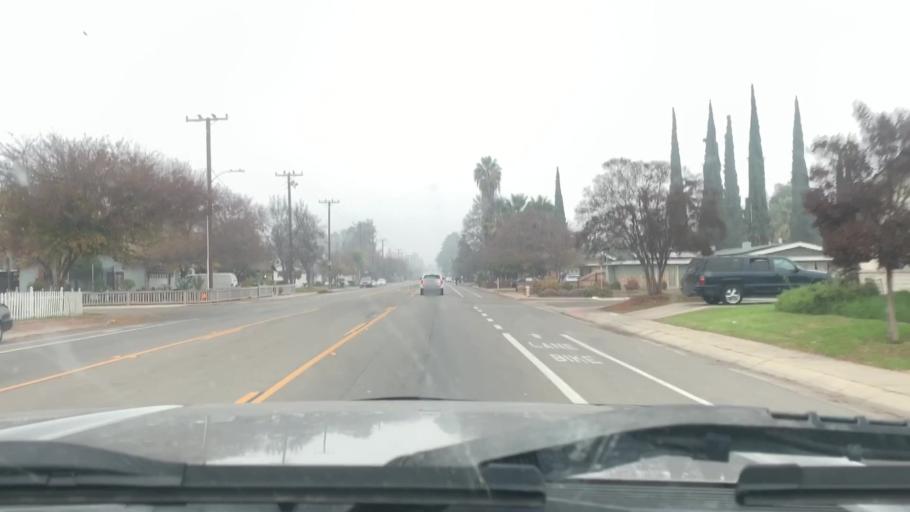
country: US
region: California
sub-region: Tulare County
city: Visalia
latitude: 36.3144
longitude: -119.3053
